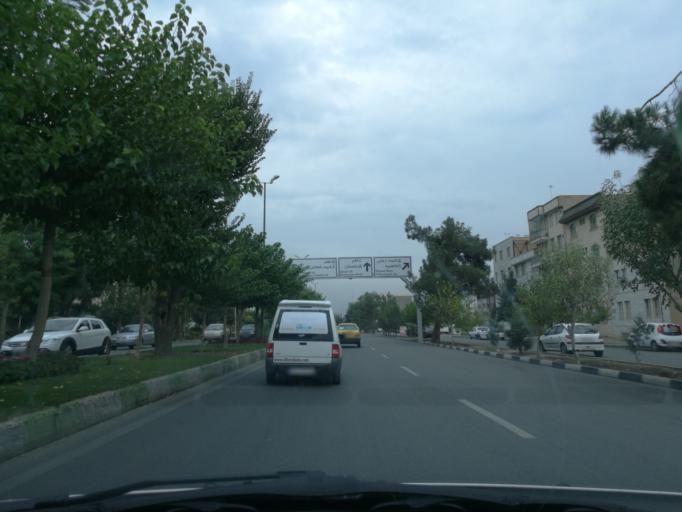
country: IR
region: Alborz
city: Karaj
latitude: 35.8586
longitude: 50.9462
